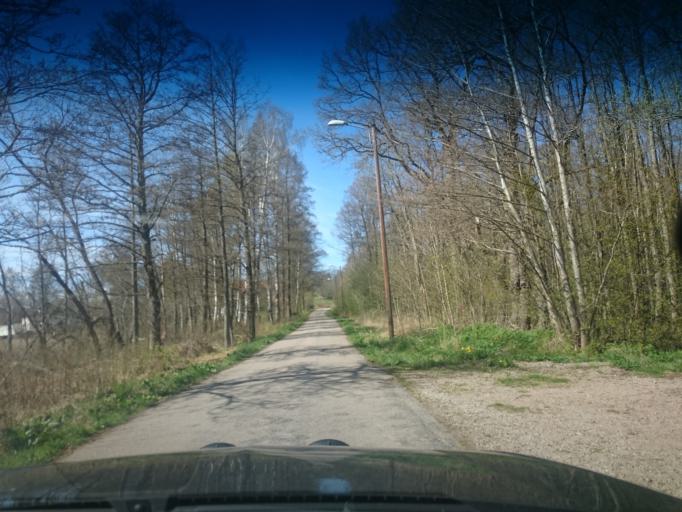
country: SE
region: Kalmar
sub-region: Hultsfreds Kommun
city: Virserum
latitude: 57.3667
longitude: 15.3955
